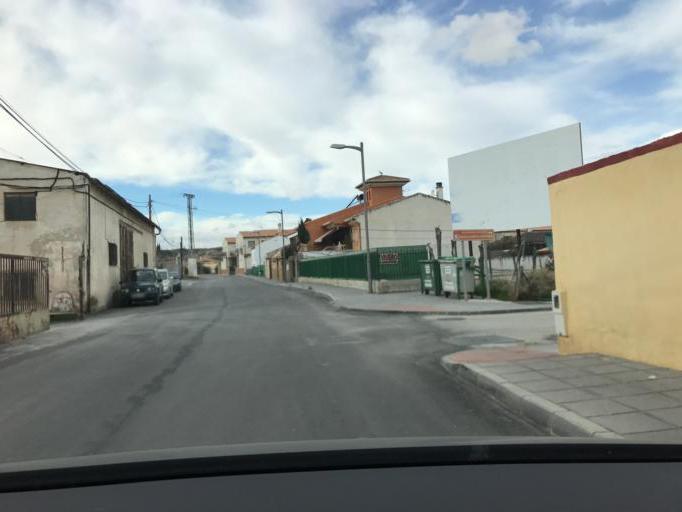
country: ES
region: Andalusia
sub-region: Provincia de Granada
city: Alhendin
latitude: 37.1036
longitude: -3.6488
